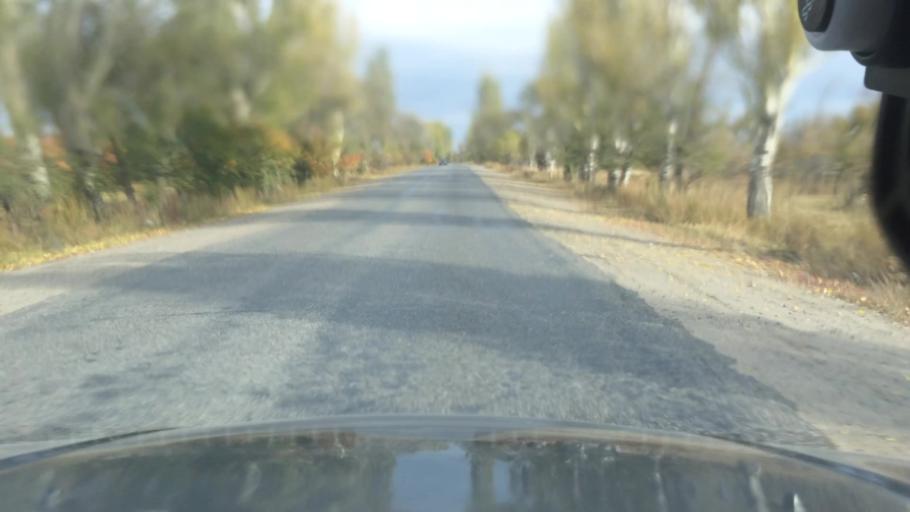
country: KG
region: Ysyk-Koel
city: Karakol
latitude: 42.5698
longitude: 78.3910
